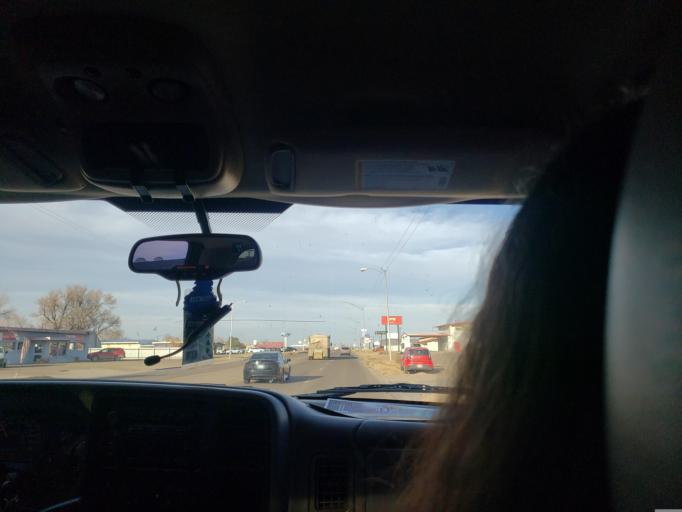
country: US
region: Oklahoma
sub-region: Texas County
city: Guymon
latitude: 36.6854
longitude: -101.4690
